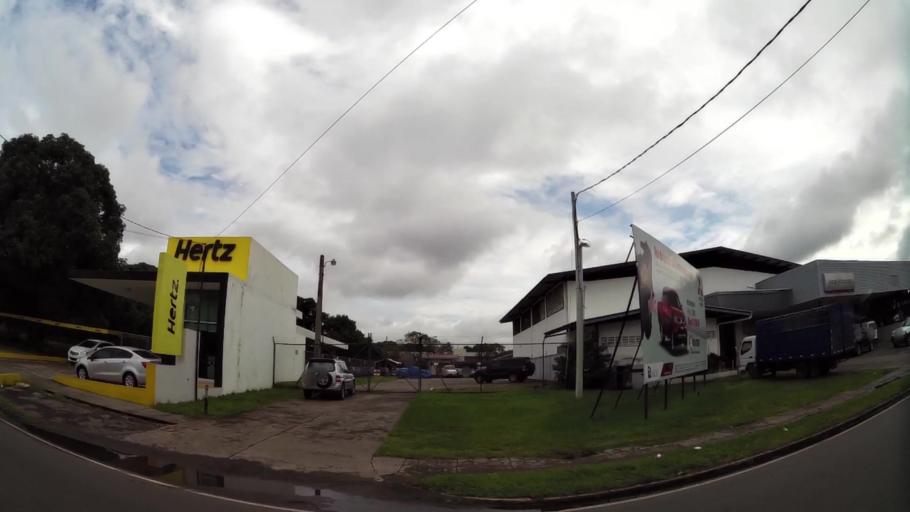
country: PA
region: Chiriqui
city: David
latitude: 8.4246
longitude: -82.4332
